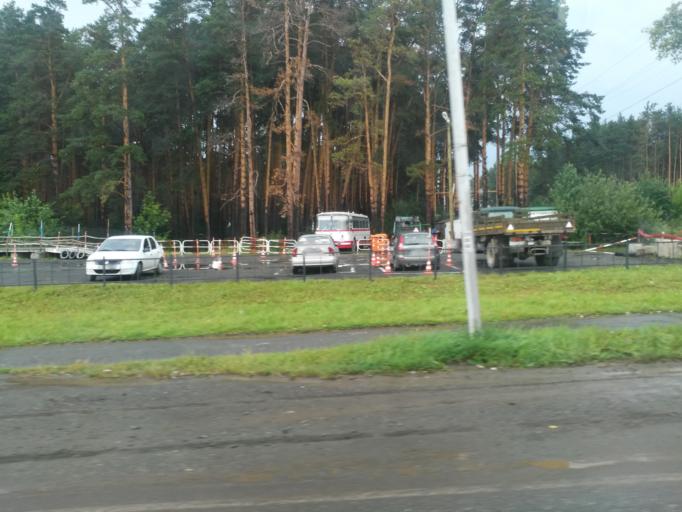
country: RU
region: Sverdlovsk
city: Shirokaya Rechka
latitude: 56.8166
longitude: 60.5203
